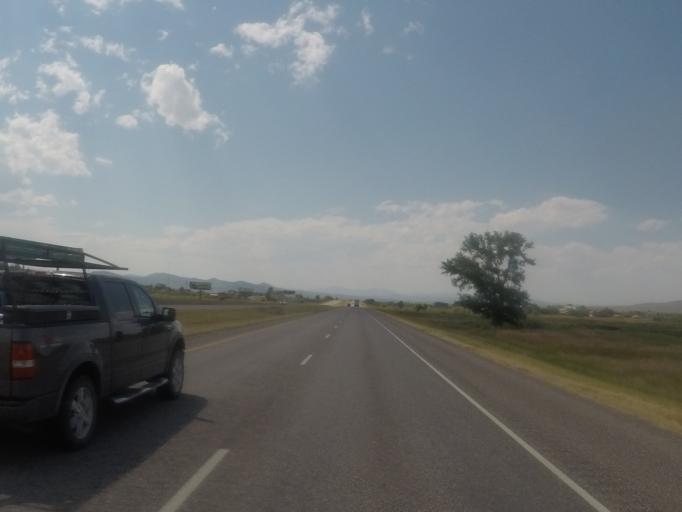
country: US
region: Montana
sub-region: Gallatin County
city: Three Forks
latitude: 45.8937
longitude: -111.4831
